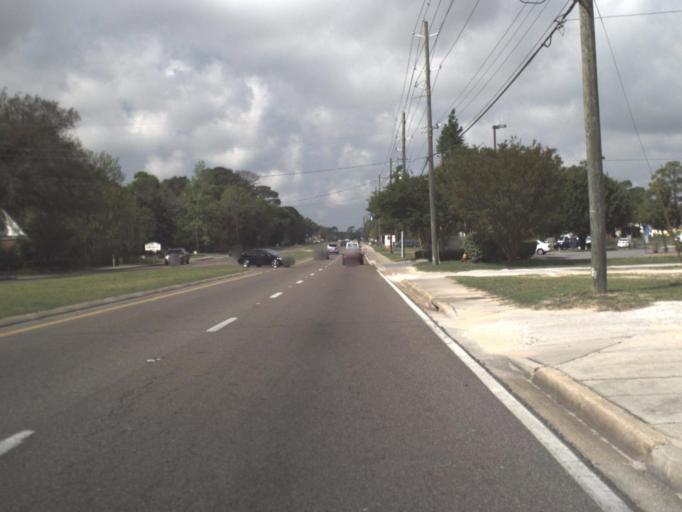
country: US
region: Florida
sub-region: Okaloosa County
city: Wright
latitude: 30.4613
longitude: -86.6281
